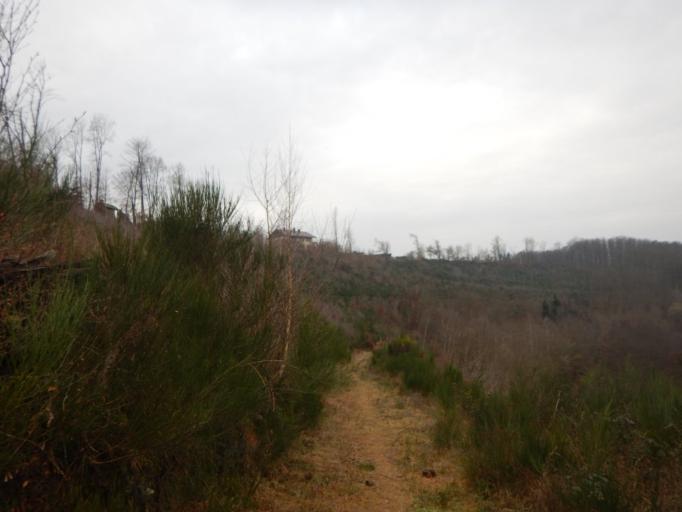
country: LU
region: Luxembourg
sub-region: Canton de Capellen
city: Koerich
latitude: 49.6777
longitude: 5.9449
